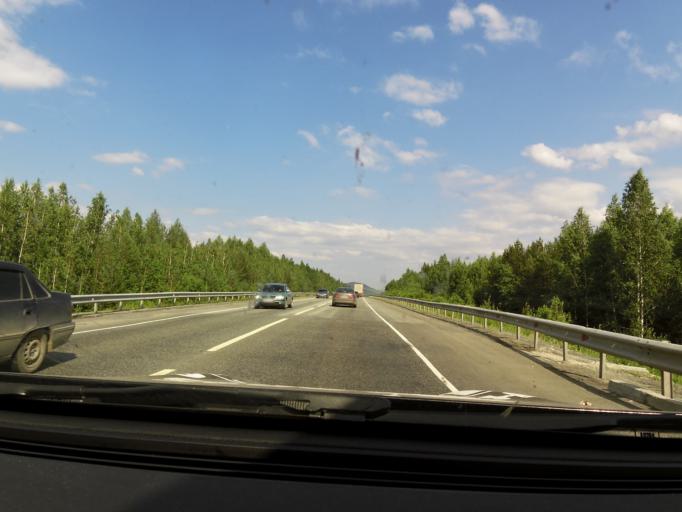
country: RU
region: Sverdlovsk
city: Revda
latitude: 56.8268
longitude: 59.9058
